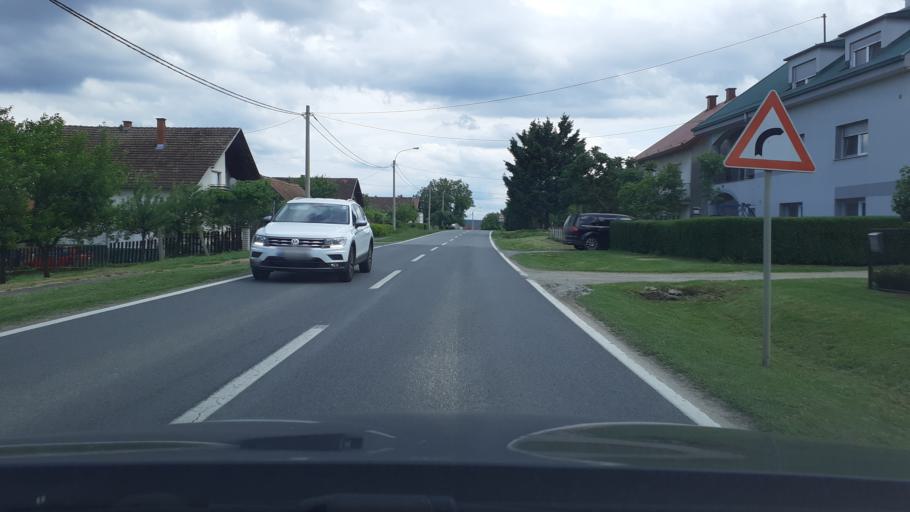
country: HR
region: Pozesko-Slavonska
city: Pleternica
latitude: 45.3087
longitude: 17.7859
